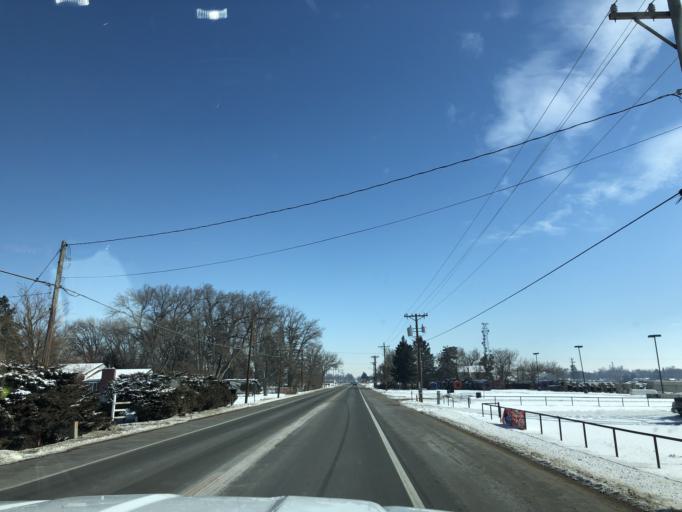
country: US
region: Colorado
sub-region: Morgan County
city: Fort Morgan
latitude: 40.2539
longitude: -103.8228
